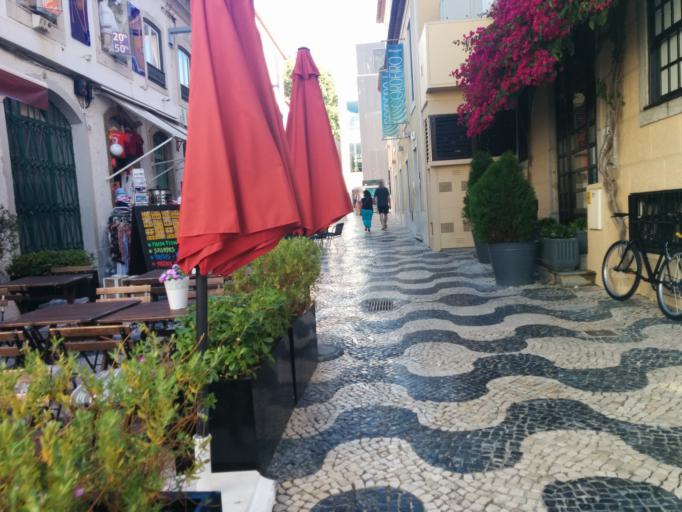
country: PT
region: Lisbon
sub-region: Cascais
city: Cascais
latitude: 38.6987
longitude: -9.4201
